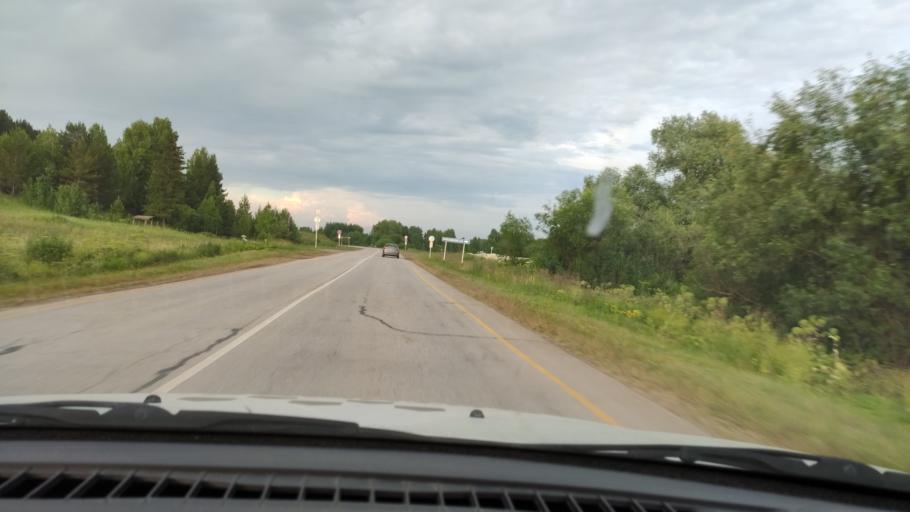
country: RU
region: Perm
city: Kukushtan
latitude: 57.4860
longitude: 56.6125
